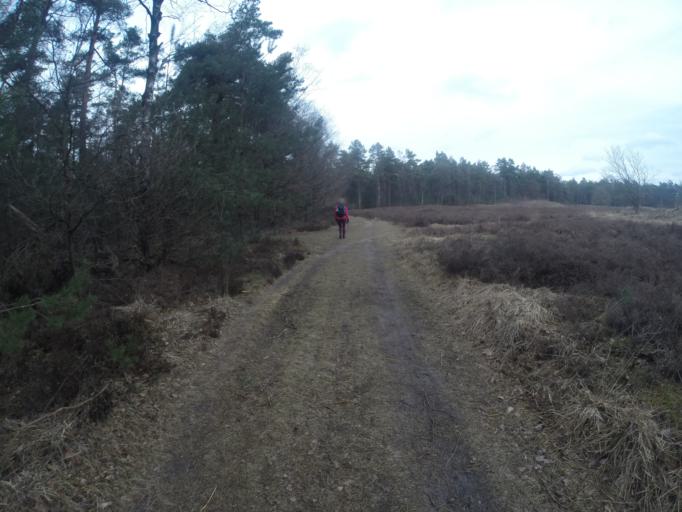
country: NL
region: Gelderland
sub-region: Gemeente Bronckhorst
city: Zelhem
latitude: 52.0425
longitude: 6.3843
